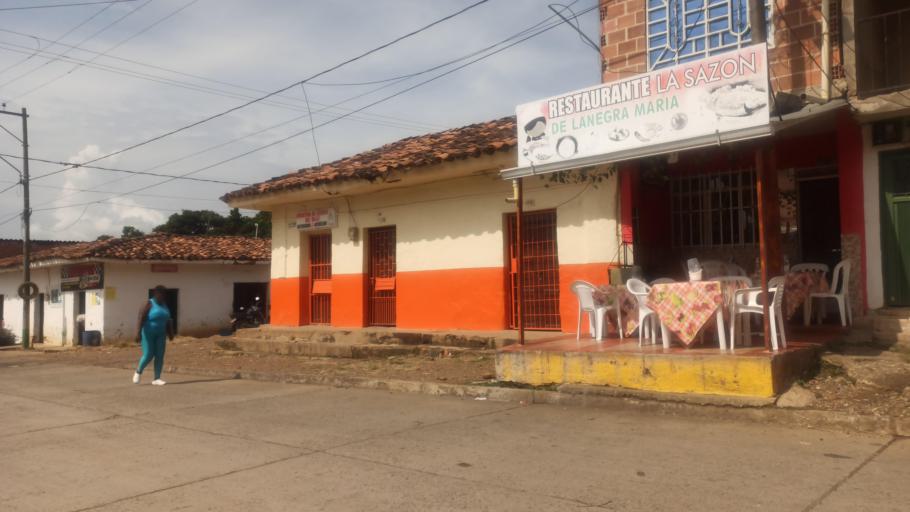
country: CO
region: Cauca
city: Buenos Aires
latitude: 3.1289
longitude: -76.5944
